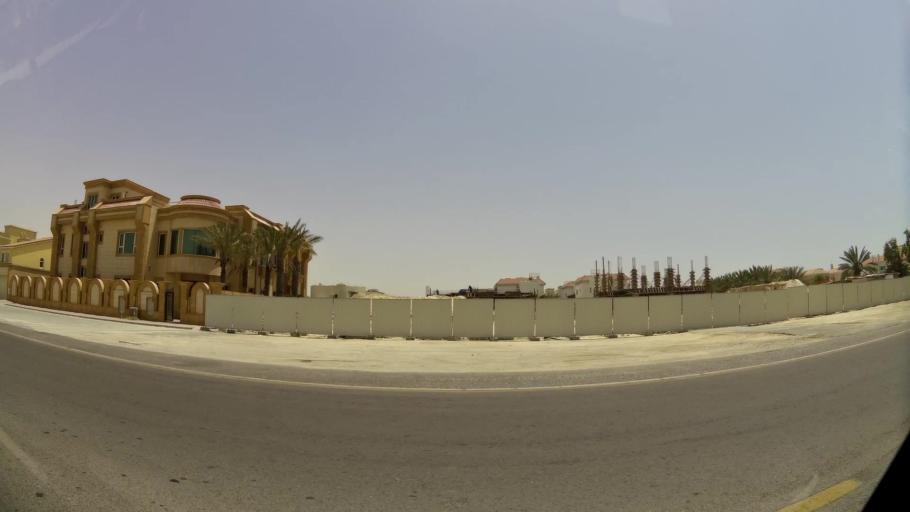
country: AE
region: Dubai
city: Dubai
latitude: 25.1580
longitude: 55.2110
